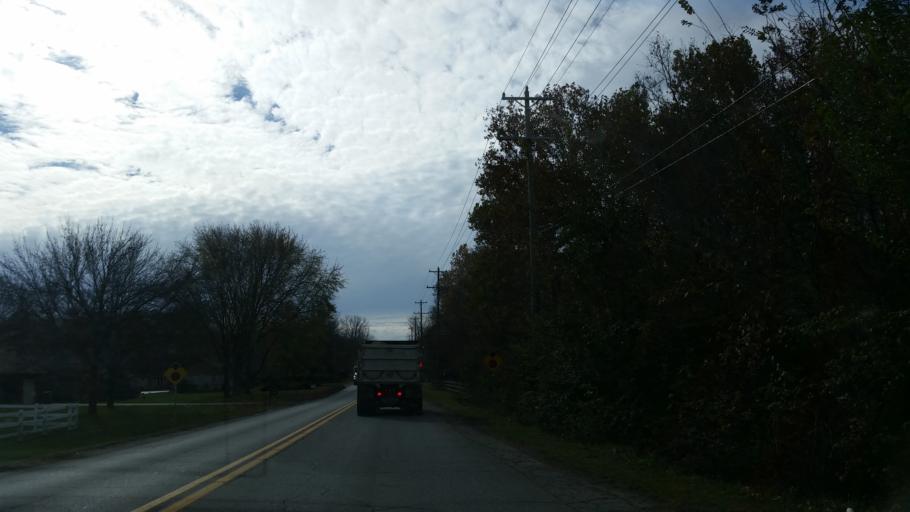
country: US
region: Indiana
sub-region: Howard County
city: Indian Heights
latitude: 40.4352
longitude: -86.1652
